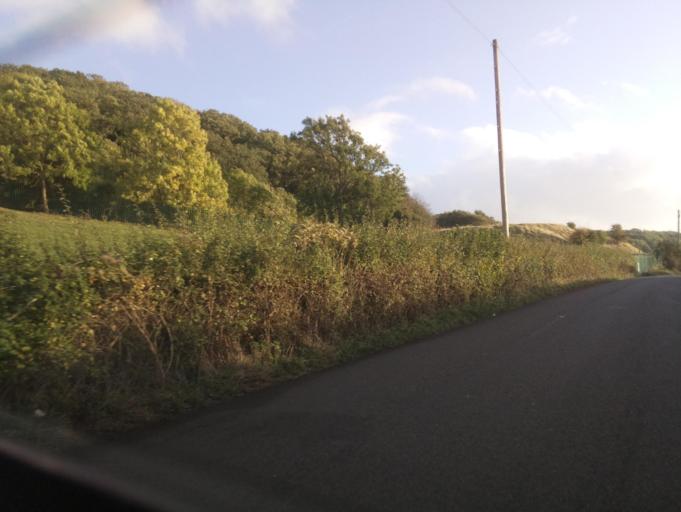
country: GB
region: England
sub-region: South Gloucestershire
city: Severn Beach
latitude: 51.5287
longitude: -2.6366
